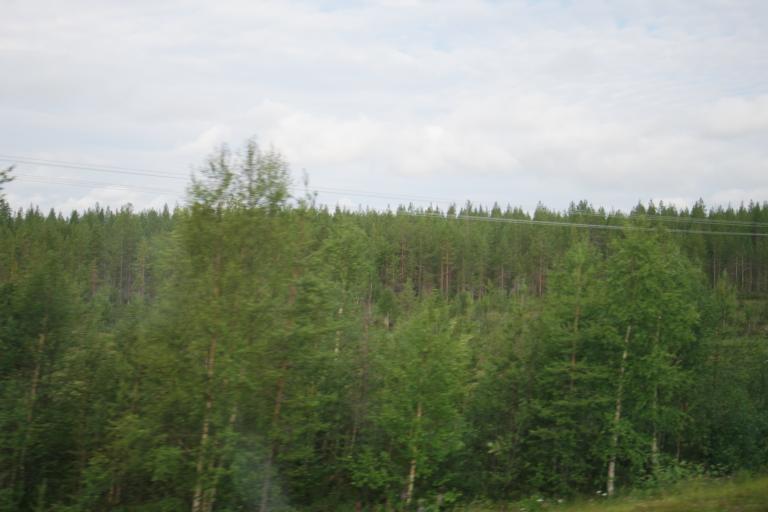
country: FI
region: Lapland
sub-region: Pohjois-Lappi
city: Sodankylae
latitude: 67.4610
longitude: 26.5890
